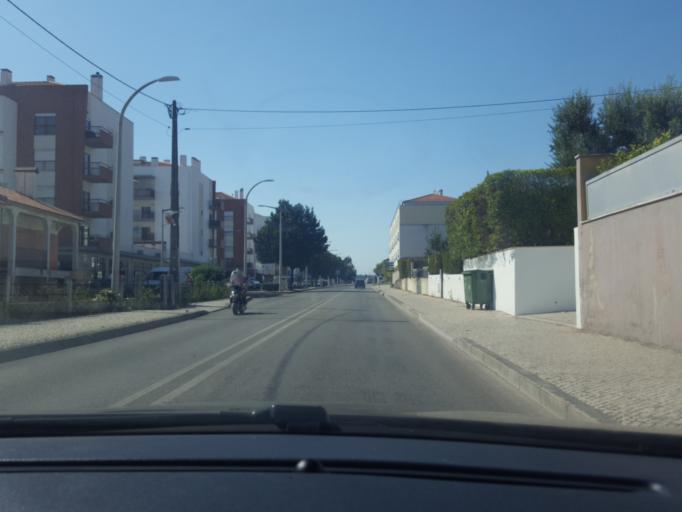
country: PT
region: Leiria
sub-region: Leiria
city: Leiria
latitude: 39.7536
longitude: -8.8178
